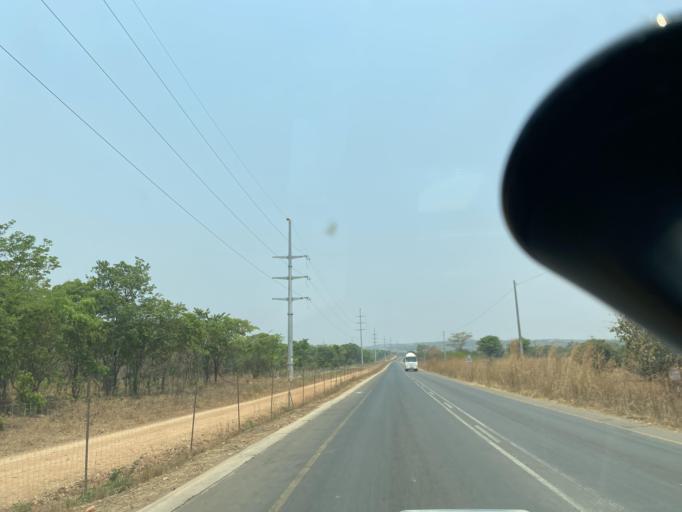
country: ZM
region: Lusaka
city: Lusaka
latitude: -15.5334
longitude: 28.4688
